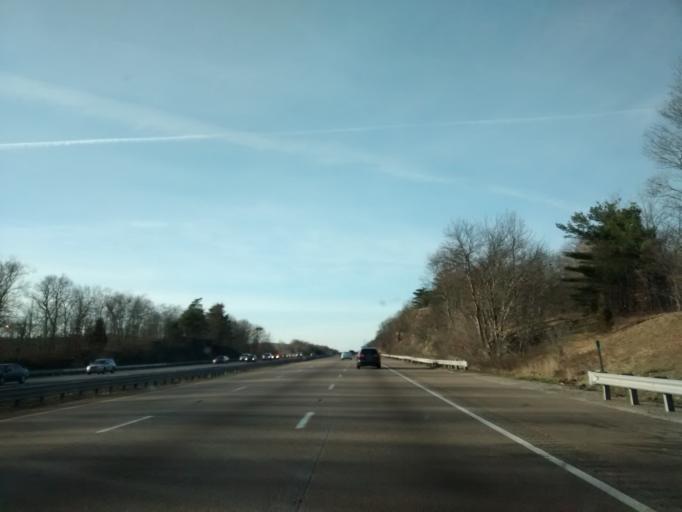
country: US
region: Massachusetts
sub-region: Norfolk County
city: Avon
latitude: 42.1310
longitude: -71.0633
